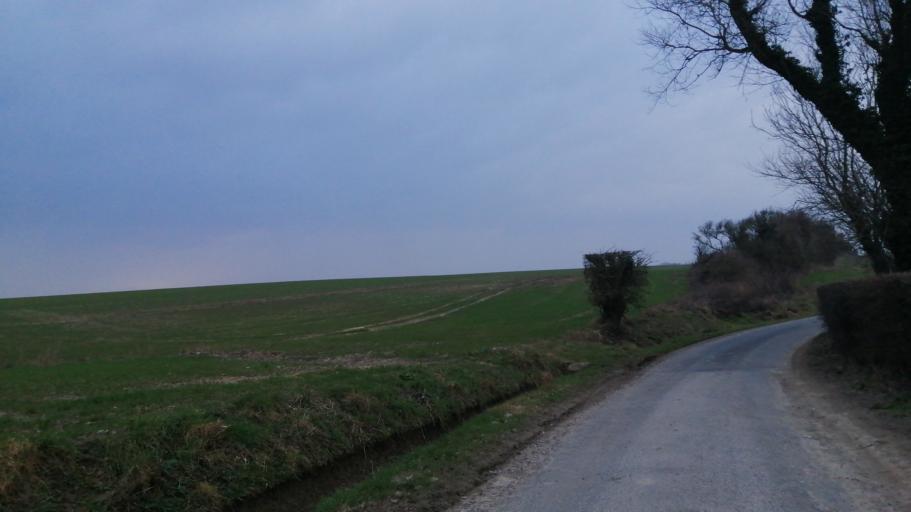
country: FR
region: Nord-Pas-de-Calais
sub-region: Departement du Pas-de-Calais
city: Wissant
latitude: 50.8793
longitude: 1.6741
